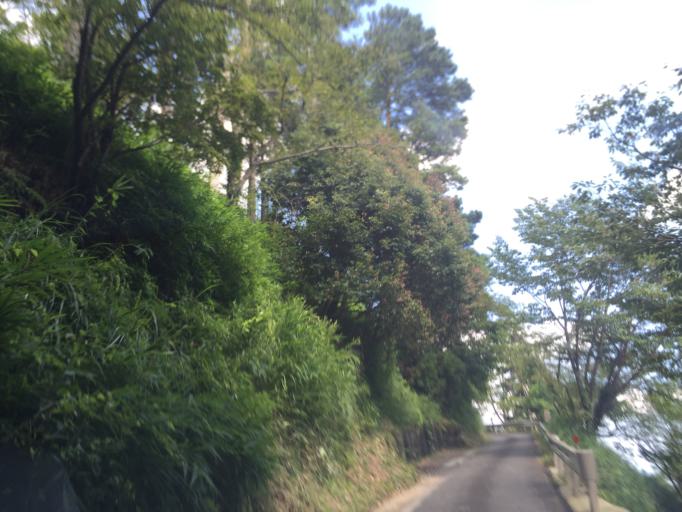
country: JP
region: Shizuoka
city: Kanaya
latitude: 34.8398
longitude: 138.0692
